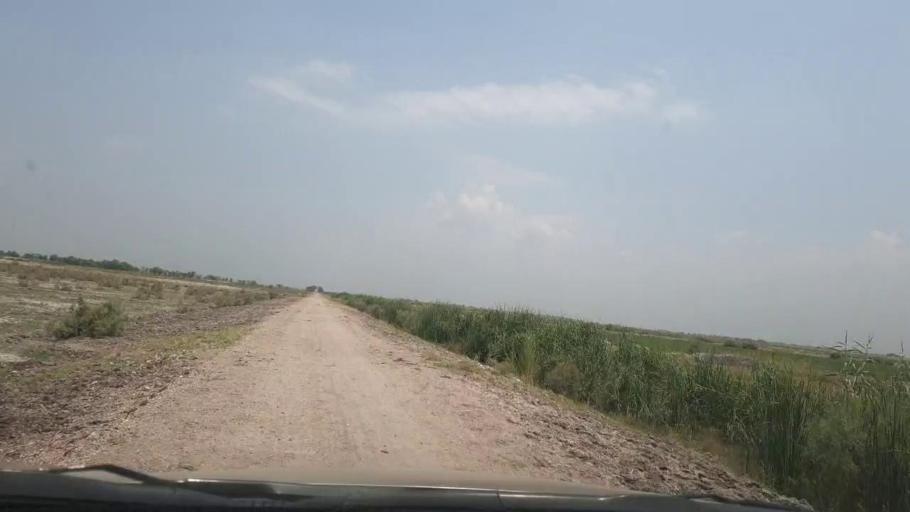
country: PK
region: Sindh
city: Naudero
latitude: 27.7187
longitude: 68.2972
